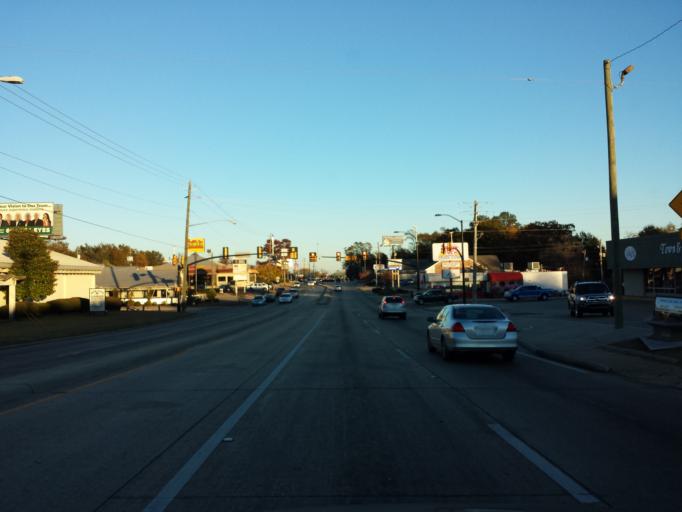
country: US
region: Mississippi
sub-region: Lamar County
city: Arnold Line
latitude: 31.3248
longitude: -89.3410
